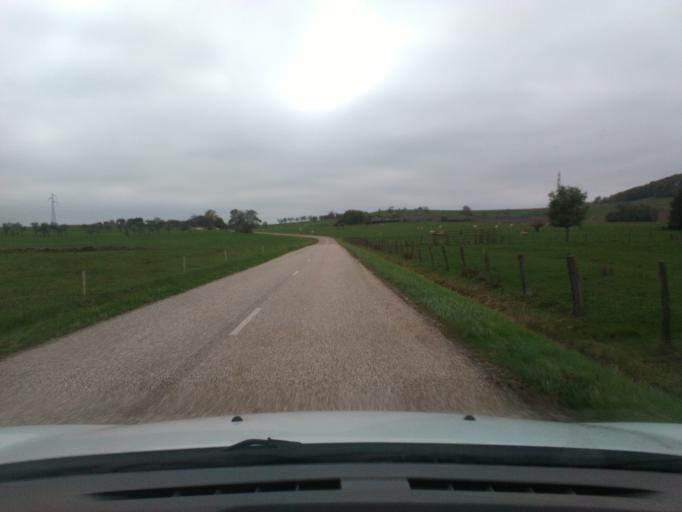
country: FR
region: Lorraine
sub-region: Departement des Vosges
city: Vincey
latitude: 48.3048
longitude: 6.3202
